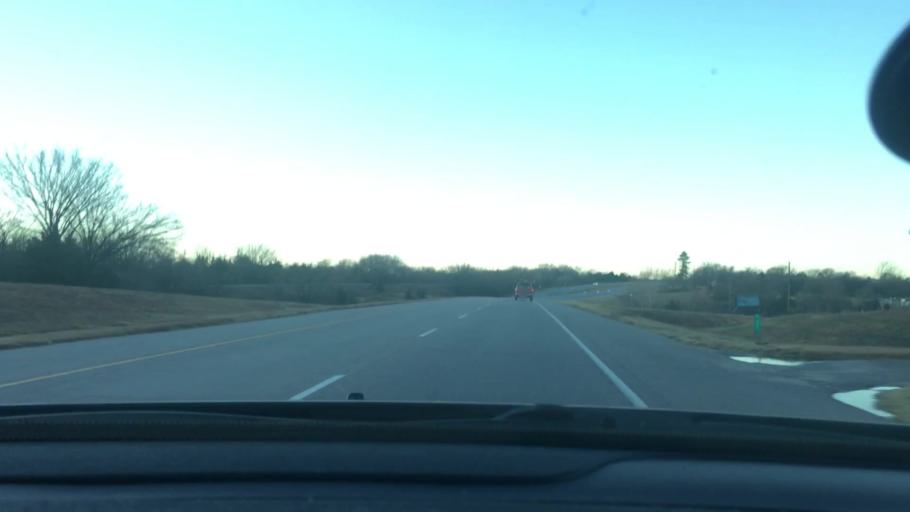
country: US
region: Oklahoma
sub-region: Pontotoc County
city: Ada
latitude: 34.7268
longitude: -96.7114
